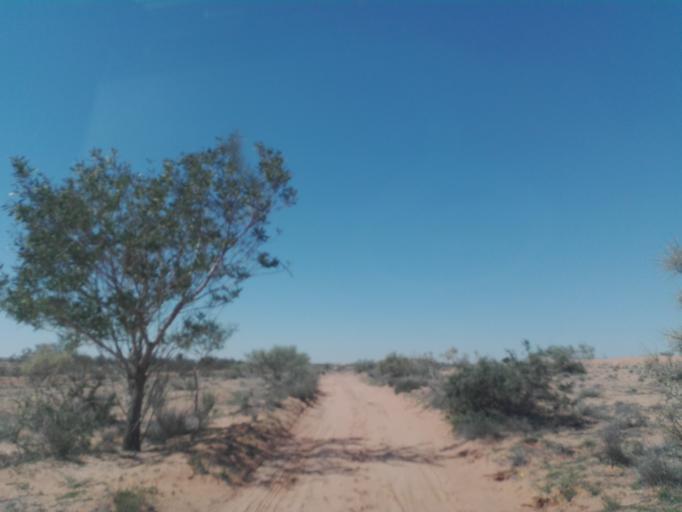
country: TN
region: Safaqis
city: Bi'r `Ali Bin Khalifah
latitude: 34.7902
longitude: 10.2760
